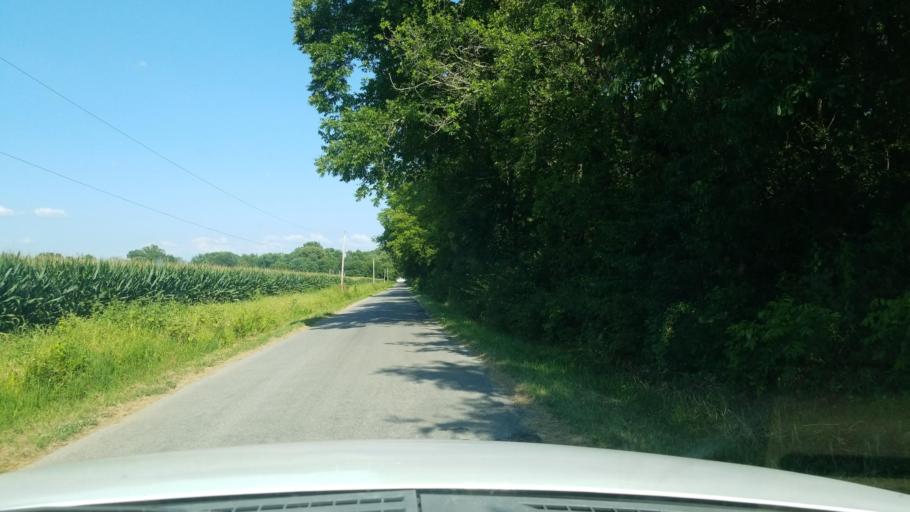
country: US
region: Illinois
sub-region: Saline County
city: Eldorado
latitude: 37.8049
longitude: -88.4656
